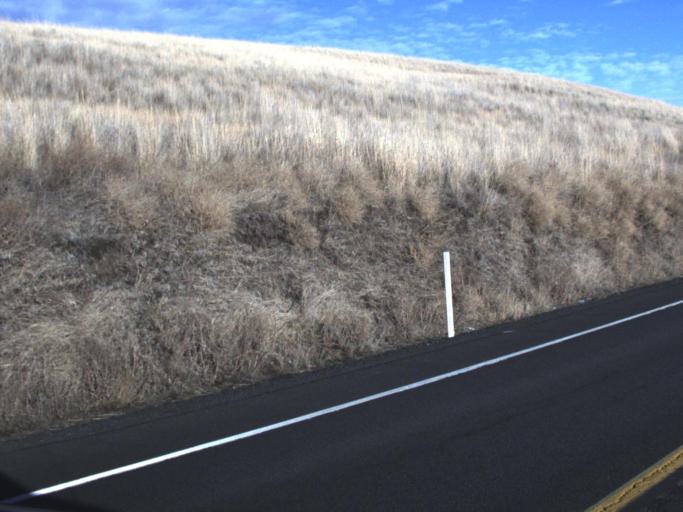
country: US
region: Washington
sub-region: Garfield County
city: Pomeroy
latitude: 46.7035
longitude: -117.7863
